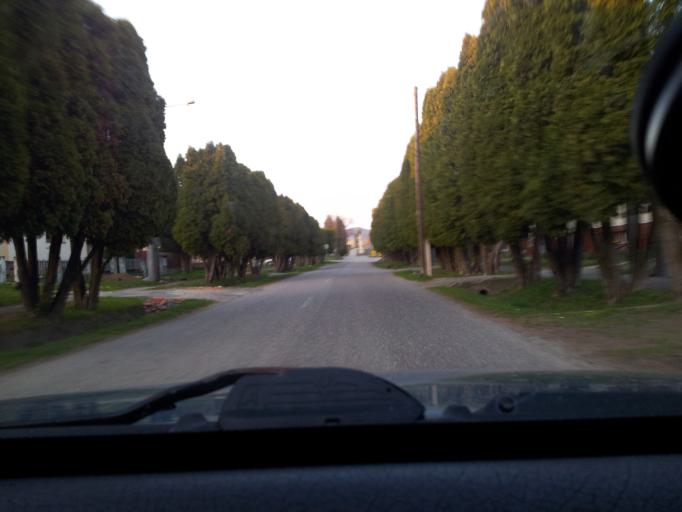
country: SK
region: Nitriansky
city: Tlmace
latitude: 48.3216
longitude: 18.5269
